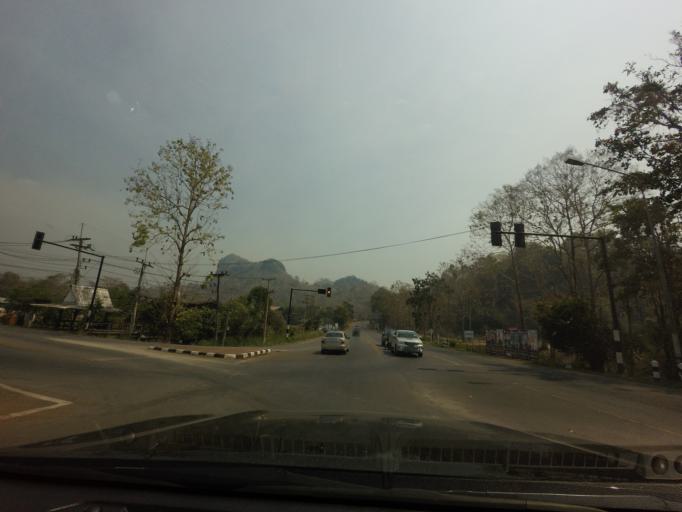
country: TH
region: Kanchanaburi
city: Thong Pha Phum
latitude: 14.7374
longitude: 98.6402
